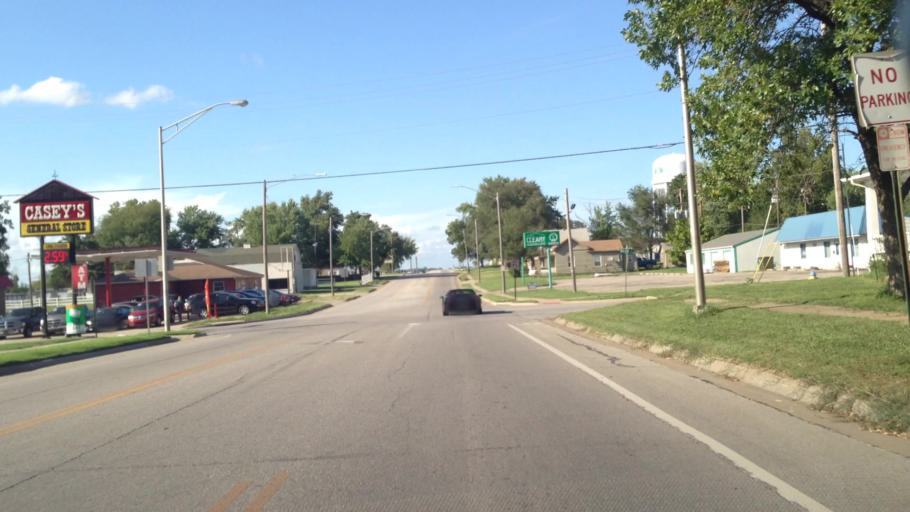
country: US
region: Kansas
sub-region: Franklin County
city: Ottawa
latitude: 38.6299
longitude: -95.2677
